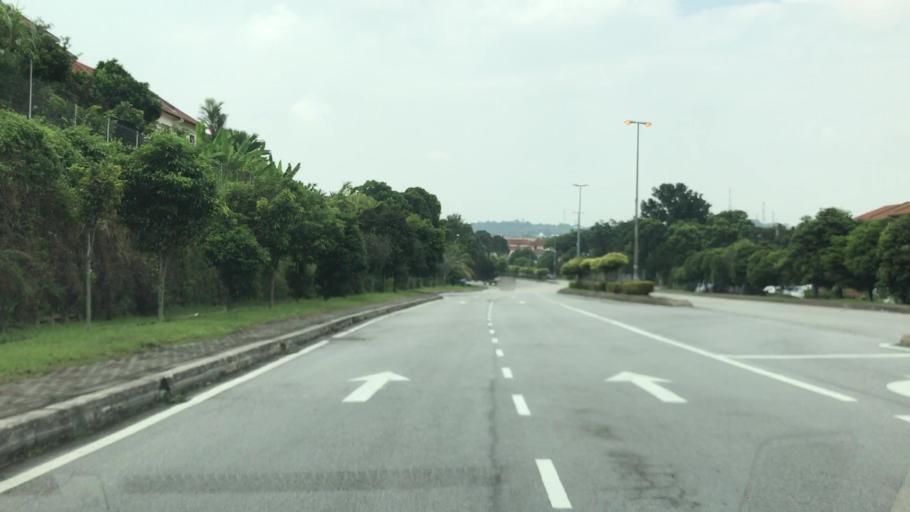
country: MY
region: Putrajaya
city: Putrajaya
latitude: 2.9874
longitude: 101.6654
